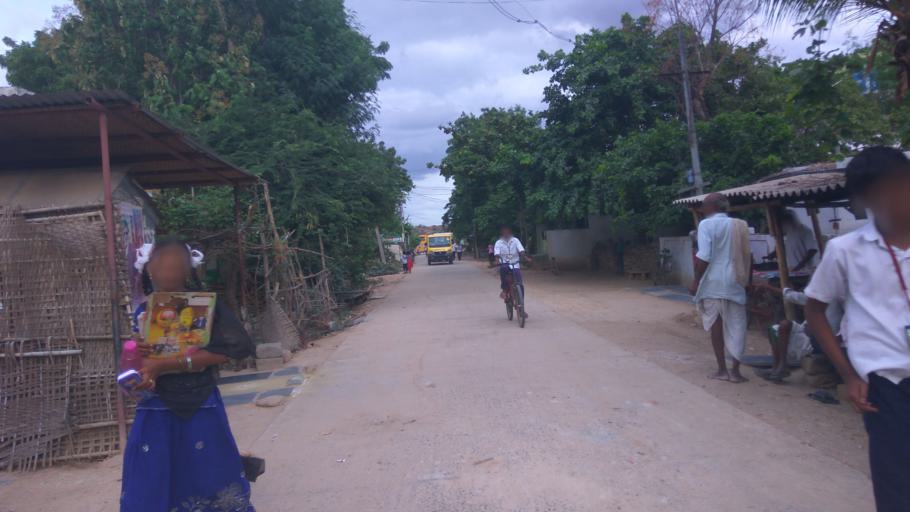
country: IN
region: Andhra Pradesh
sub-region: Prakasam
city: Cumbum
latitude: 15.5905
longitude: 79.1098
